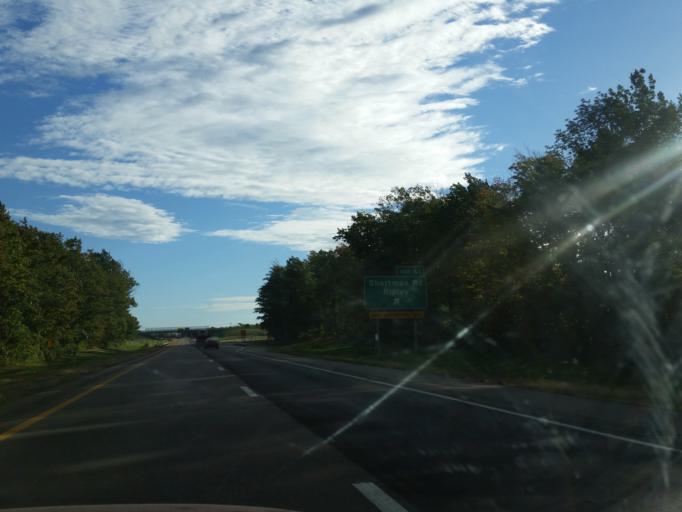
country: US
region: Pennsylvania
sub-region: Erie County
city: North East
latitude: 42.2589
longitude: -79.7504
